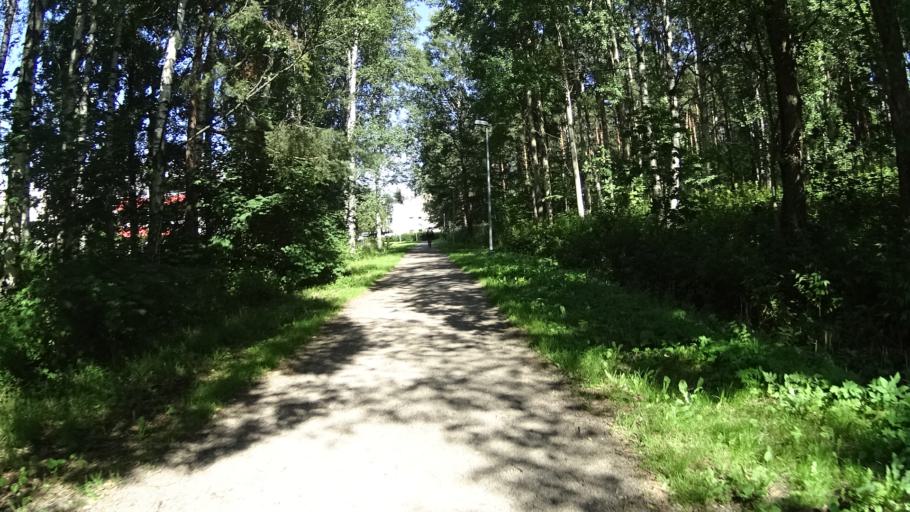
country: FI
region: Uusimaa
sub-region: Helsinki
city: Teekkarikylae
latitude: 60.2376
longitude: 24.8695
